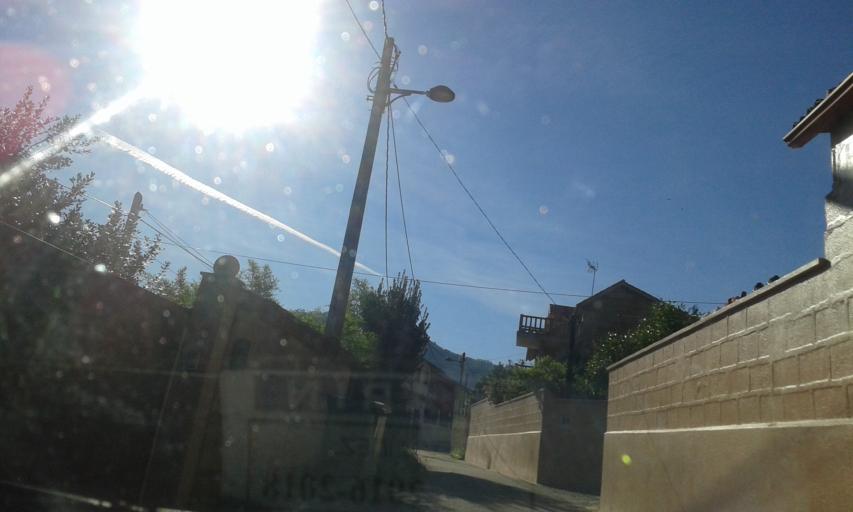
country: ES
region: Galicia
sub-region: Provincia de Pontevedra
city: Marin
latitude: 42.3596
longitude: -8.7424
